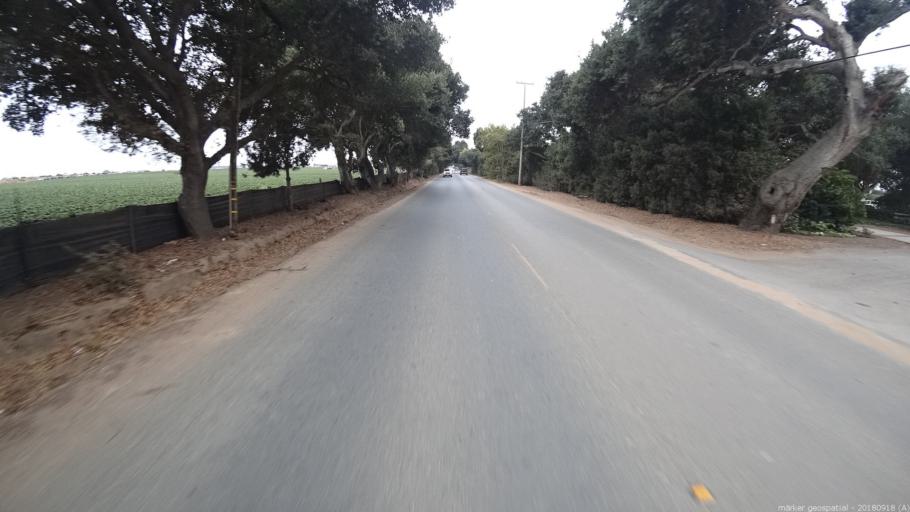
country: US
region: California
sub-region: Monterey County
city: Prunedale
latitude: 36.7434
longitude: -121.6297
